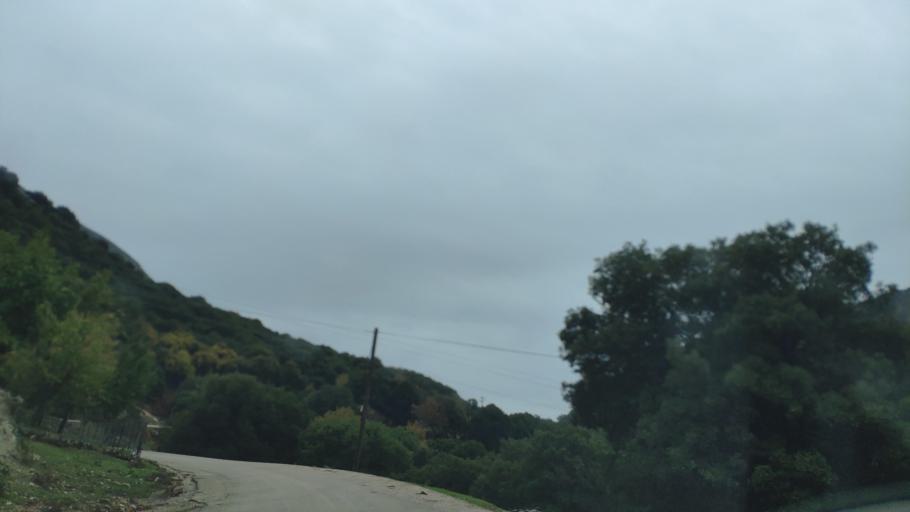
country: GR
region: Epirus
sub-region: Nomos Thesprotias
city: Paramythia
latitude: 39.3820
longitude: 20.6348
